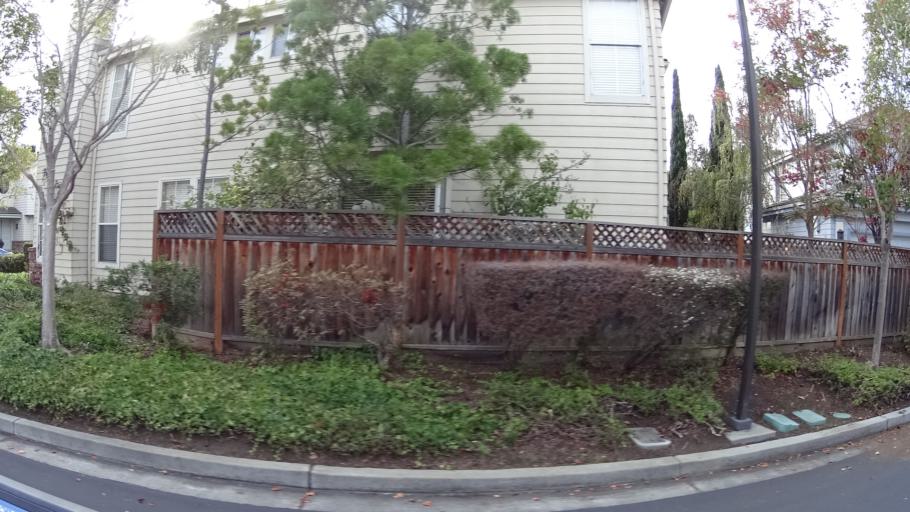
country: US
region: California
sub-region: San Mateo County
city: Redwood Shores
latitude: 37.5379
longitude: -122.2339
